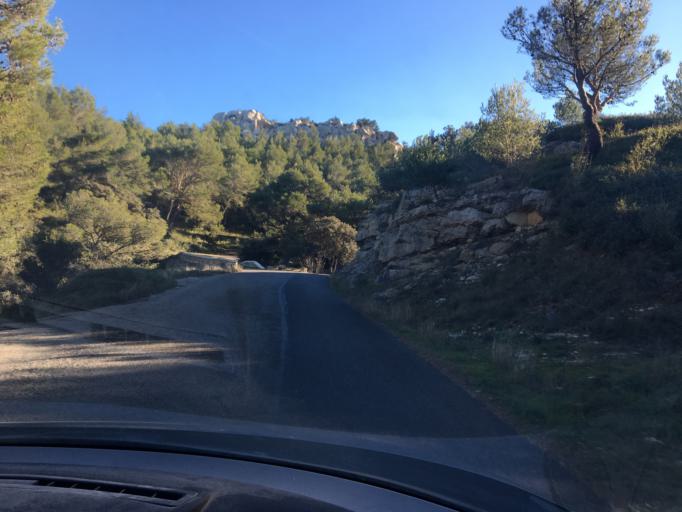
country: FR
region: Provence-Alpes-Cote d'Azur
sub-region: Departement des Bouches-du-Rhone
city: Maussane-les-Alpilles
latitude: 43.7539
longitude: 4.7921
